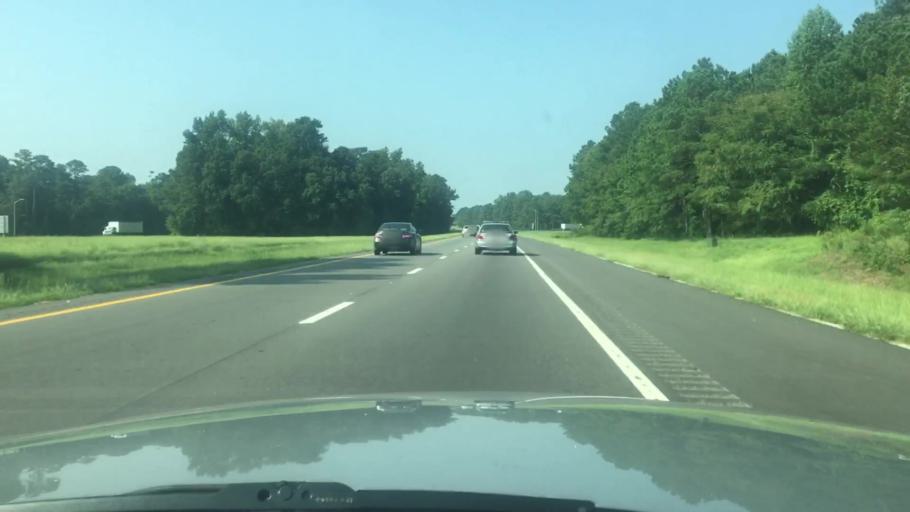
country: US
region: North Carolina
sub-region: Cumberland County
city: Vander
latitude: 34.9978
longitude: -78.8297
